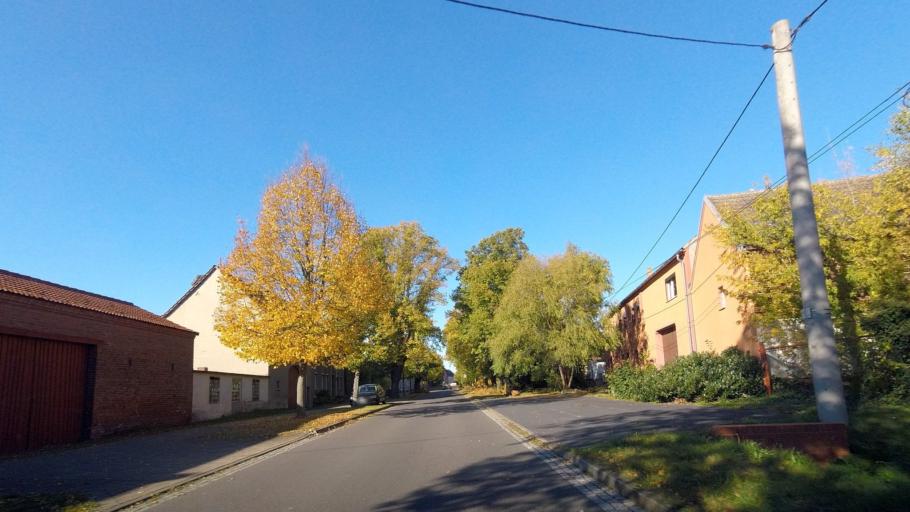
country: DE
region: Saxony-Anhalt
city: Zahna
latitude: 51.9440
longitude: 12.7845
